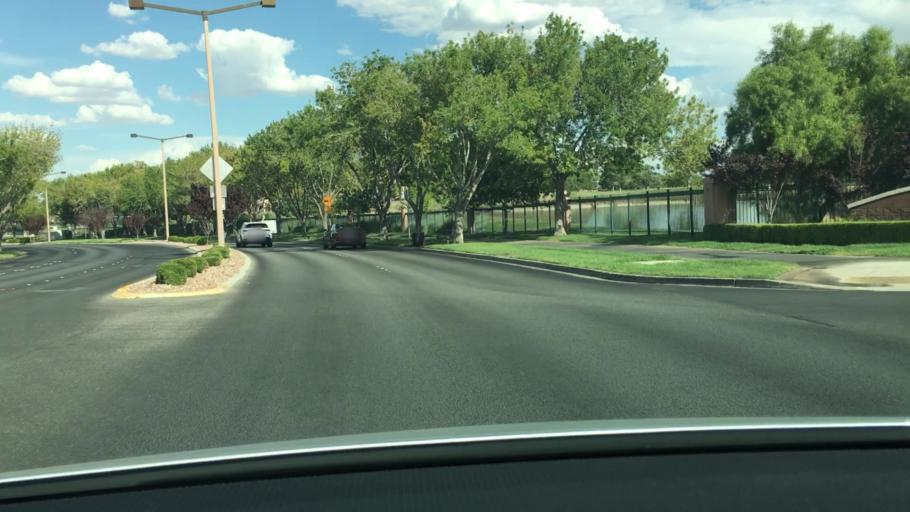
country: US
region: Nevada
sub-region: Clark County
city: Summerlin South
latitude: 36.1890
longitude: -115.3022
